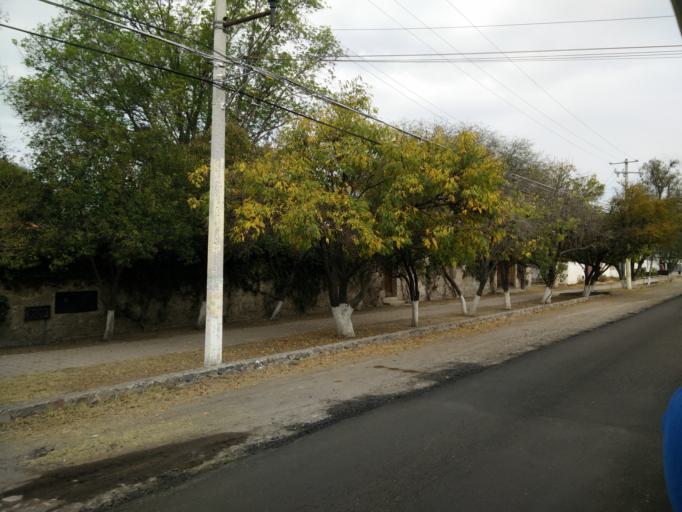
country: MX
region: Queretaro
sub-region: Tequisquiapan
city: Tequisquiapan
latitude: 20.5200
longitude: -99.8861
